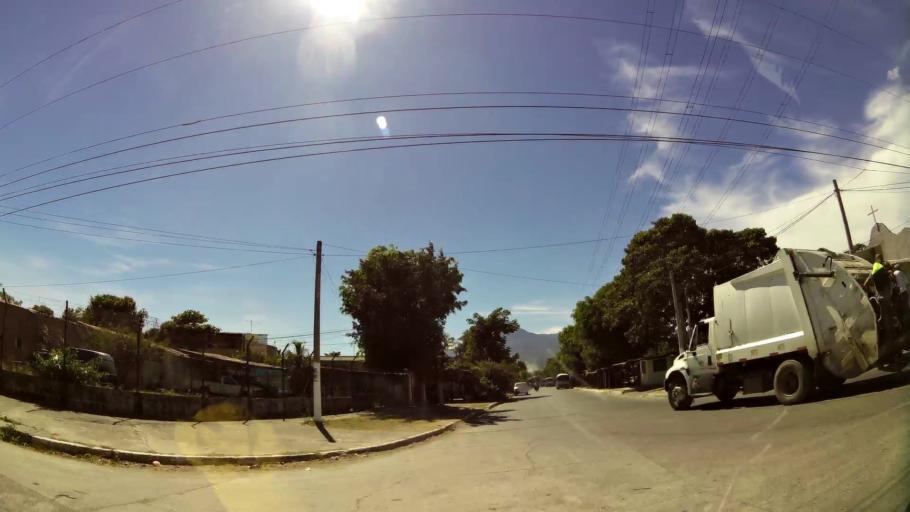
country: SV
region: San Salvador
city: Apopa
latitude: 13.8150
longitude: -89.1759
